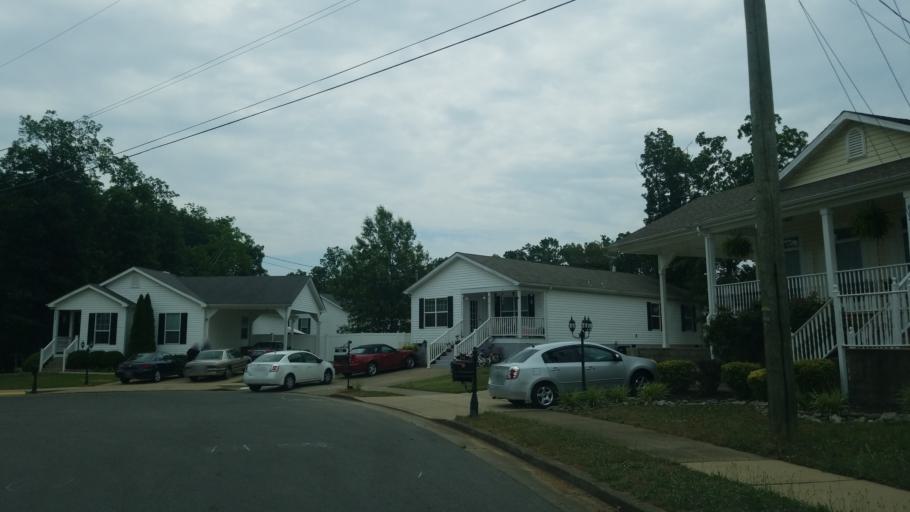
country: US
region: Tennessee
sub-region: Rutherford County
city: La Vergne
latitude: 36.0517
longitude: -86.5846
